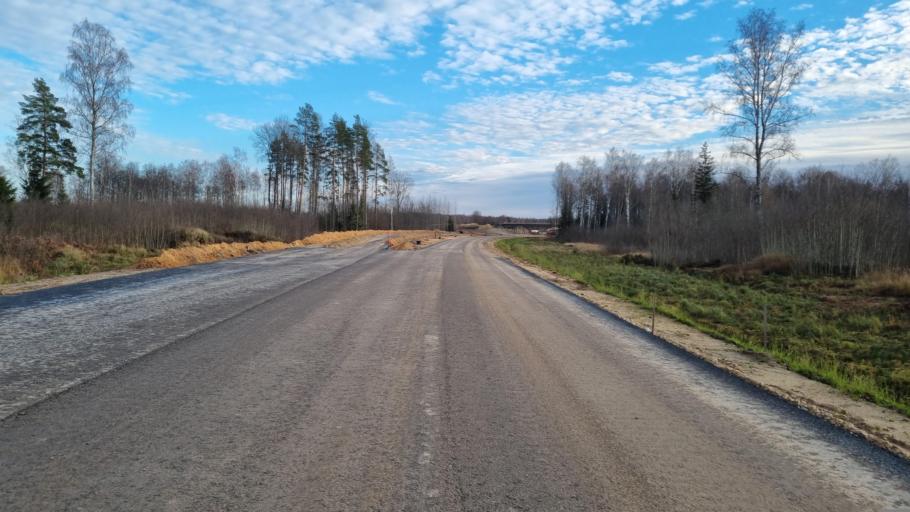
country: LV
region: Kekava
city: Kekava
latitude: 56.7823
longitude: 24.2341
